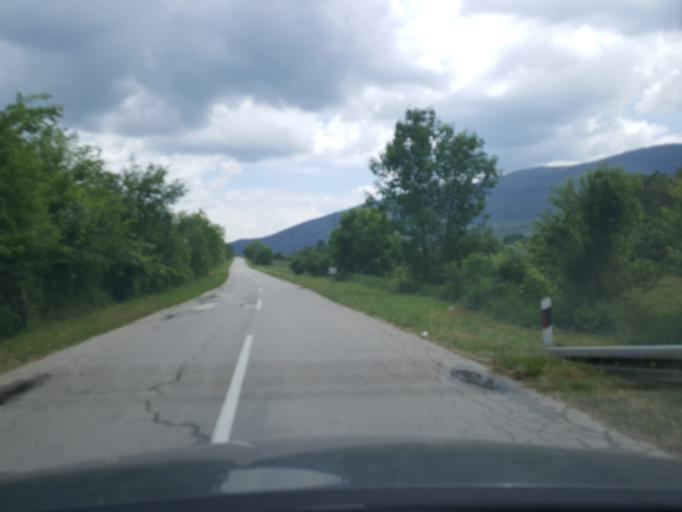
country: RS
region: Central Serbia
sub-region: Zajecarski Okrug
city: Soko Banja
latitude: 43.6438
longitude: 21.9394
